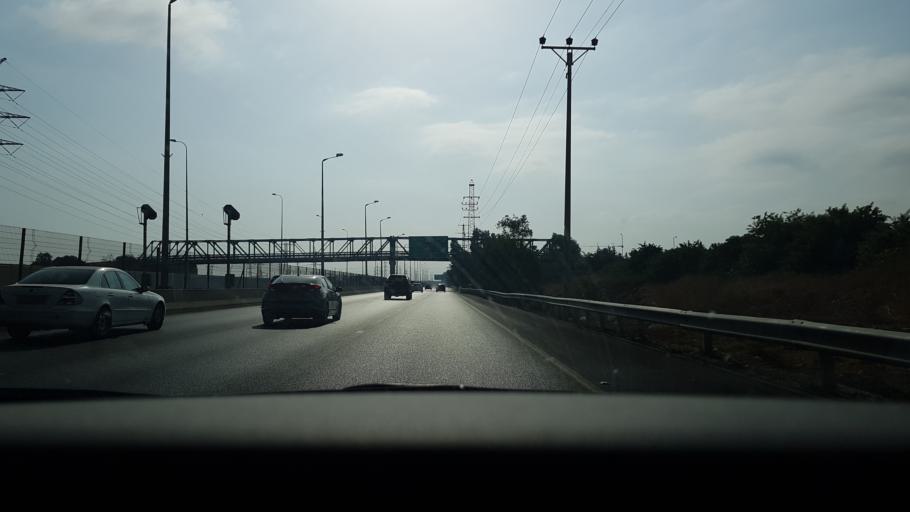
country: IL
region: Tel Aviv
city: Azor
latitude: 32.0297
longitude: 34.8051
